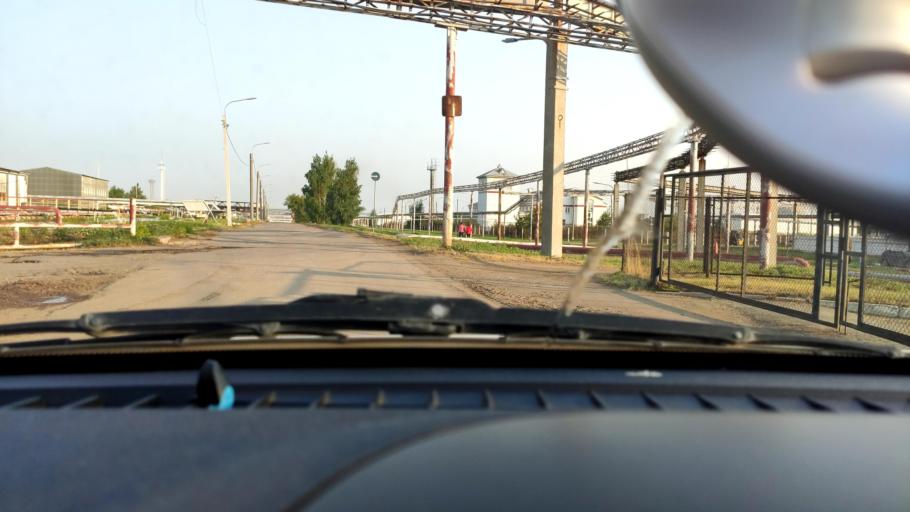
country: RU
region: Perm
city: Gamovo
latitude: 57.9080
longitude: 56.1501
